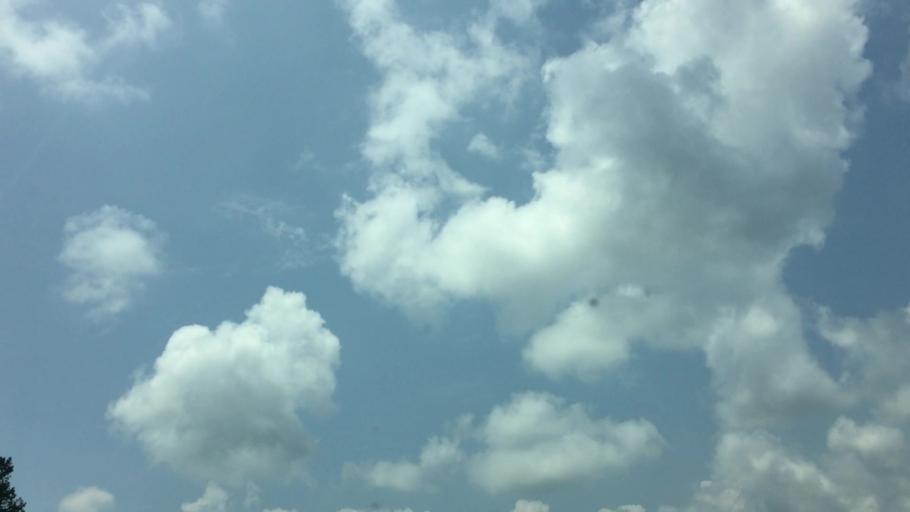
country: US
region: Georgia
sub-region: Fulton County
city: Chattahoochee Hills
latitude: 33.5796
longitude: -84.8156
